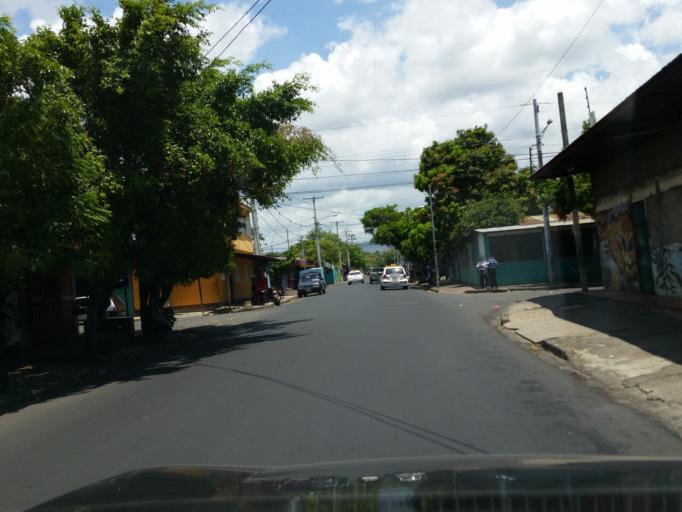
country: NI
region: Managua
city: Managua
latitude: 12.1375
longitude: -86.2536
